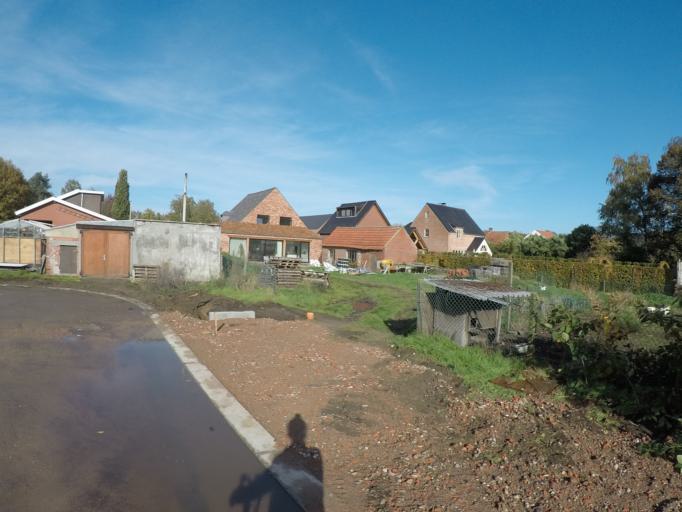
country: BE
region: Flanders
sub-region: Provincie Antwerpen
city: Zandhoven
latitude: 51.2437
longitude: 4.6374
